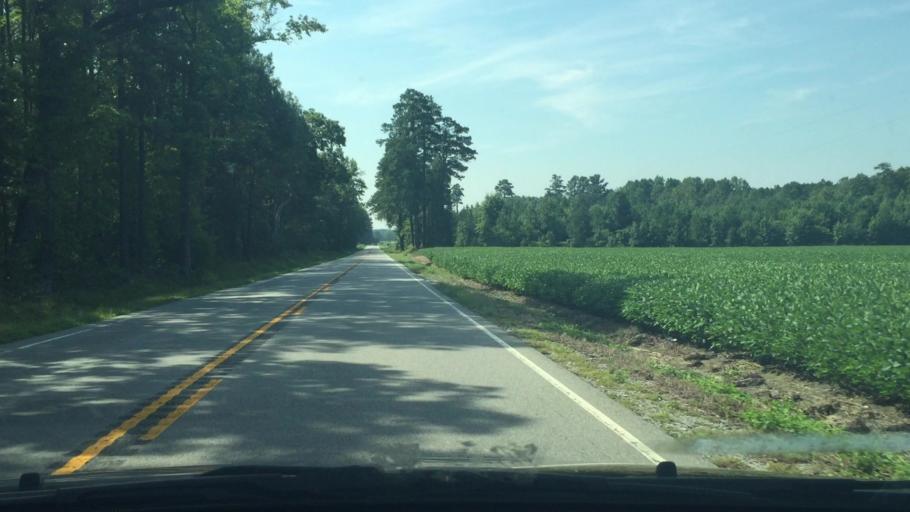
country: US
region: Virginia
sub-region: Southampton County
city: Courtland
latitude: 36.8561
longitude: -77.1354
